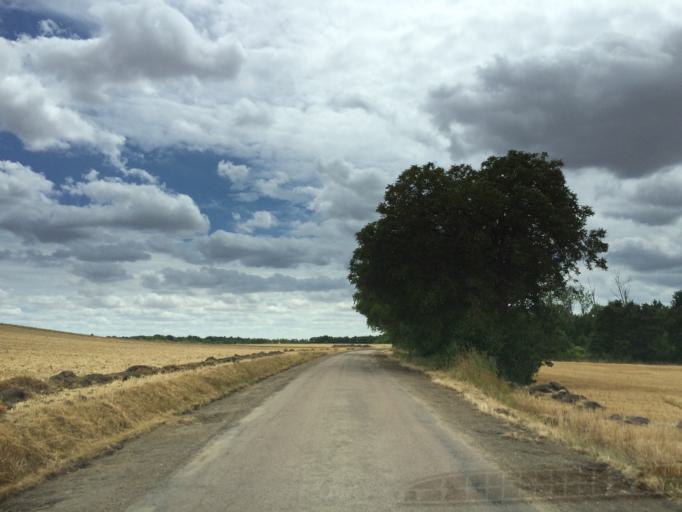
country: FR
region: Bourgogne
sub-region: Departement de l'Yonne
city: Fleury-la-Vallee
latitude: 47.8529
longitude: 3.4056
